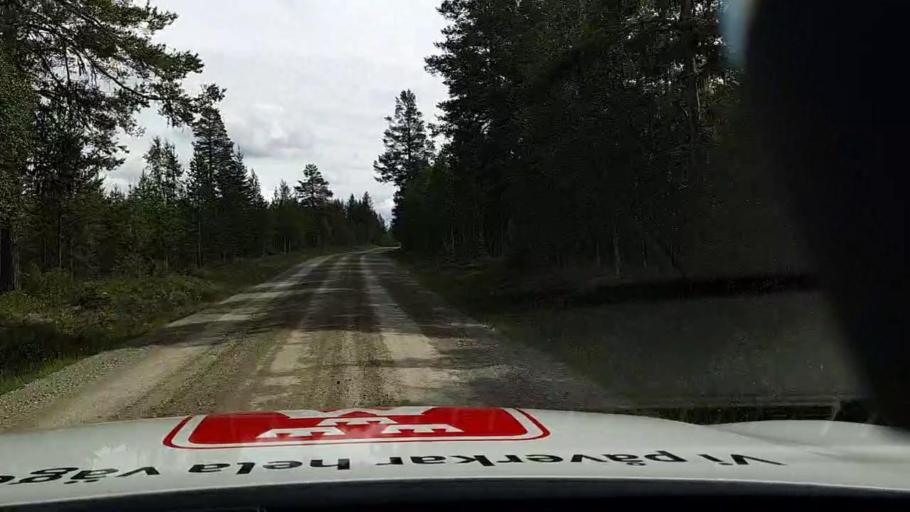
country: SE
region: Jaemtland
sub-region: Are Kommun
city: Jarpen
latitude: 62.5121
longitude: 13.4908
